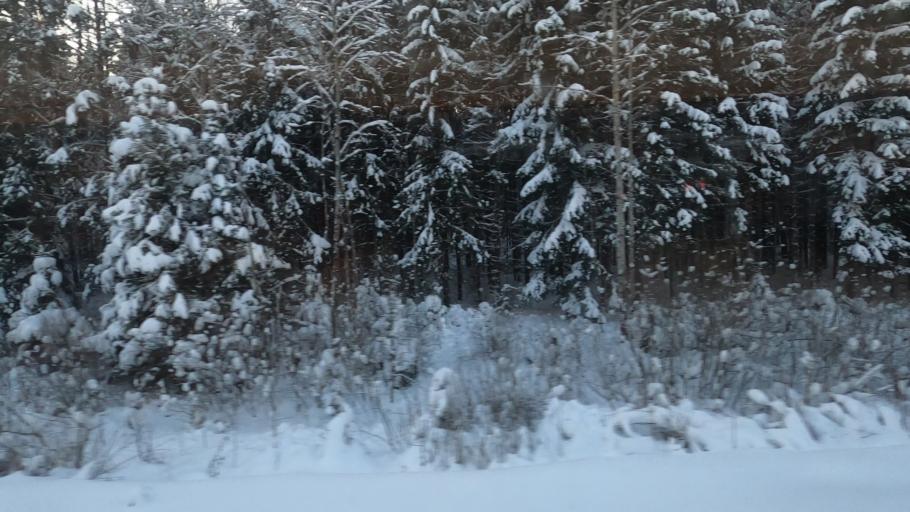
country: RU
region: Moskovskaya
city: Novo-Nikol'skoye
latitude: 56.6022
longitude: 37.5674
